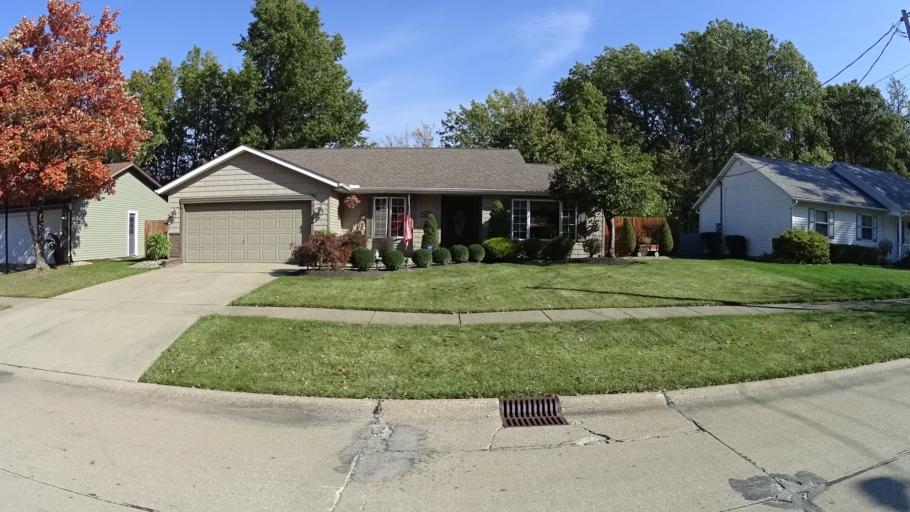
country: US
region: Ohio
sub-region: Lorain County
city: Vermilion
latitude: 41.4088
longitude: -82.3468
